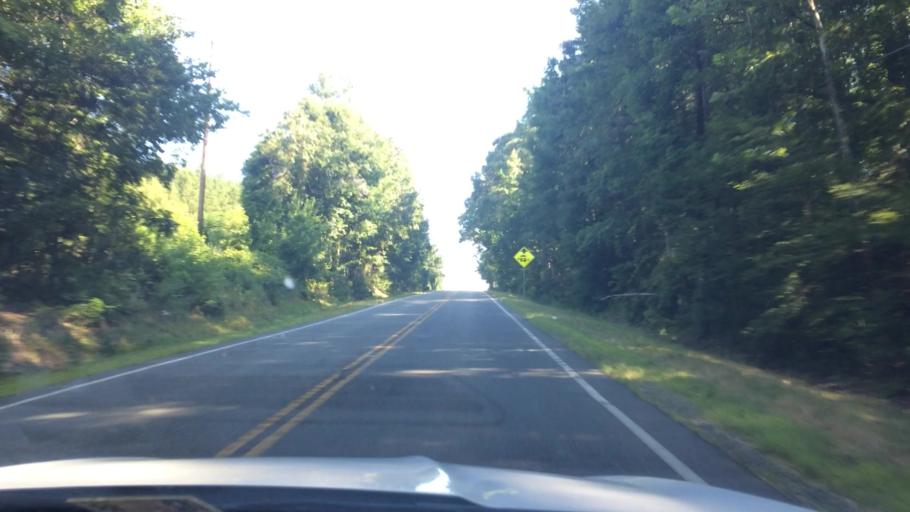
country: US
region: Virginia
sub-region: Lancaster County
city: Lancaster
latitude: 37.8342
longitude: -76.5776
